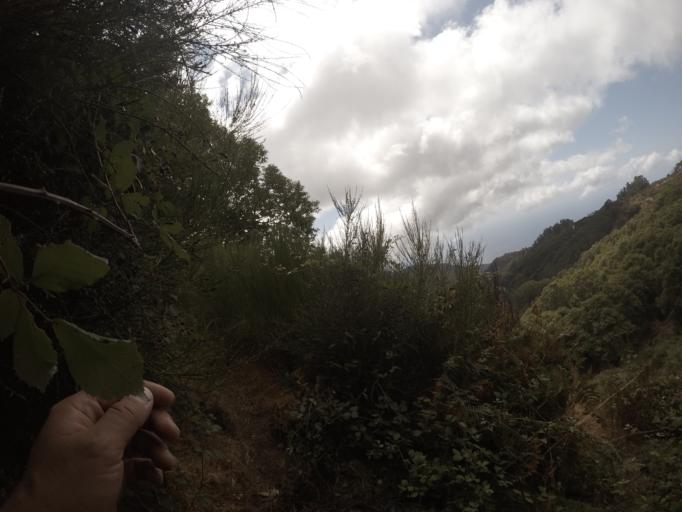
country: PT
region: Madeira
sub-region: Camara de Lobos
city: Curral das Freiras
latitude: 32.7109
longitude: -17.0040
